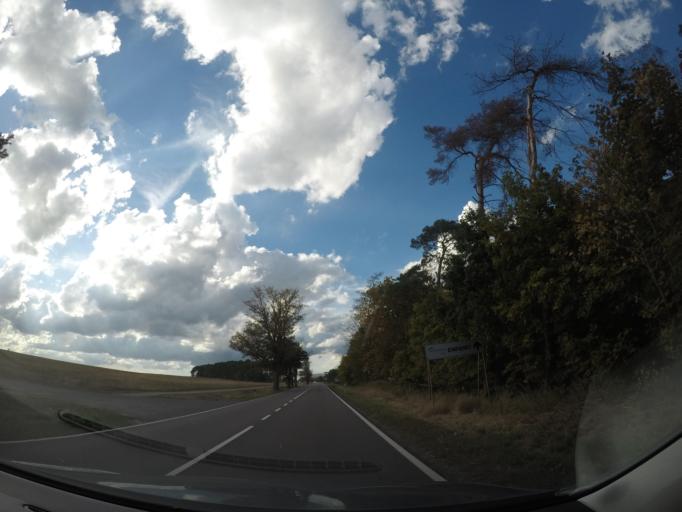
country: DE
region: Saxony-Anhalt
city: Bulstringen
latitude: 52.3055
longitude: 11.3630
